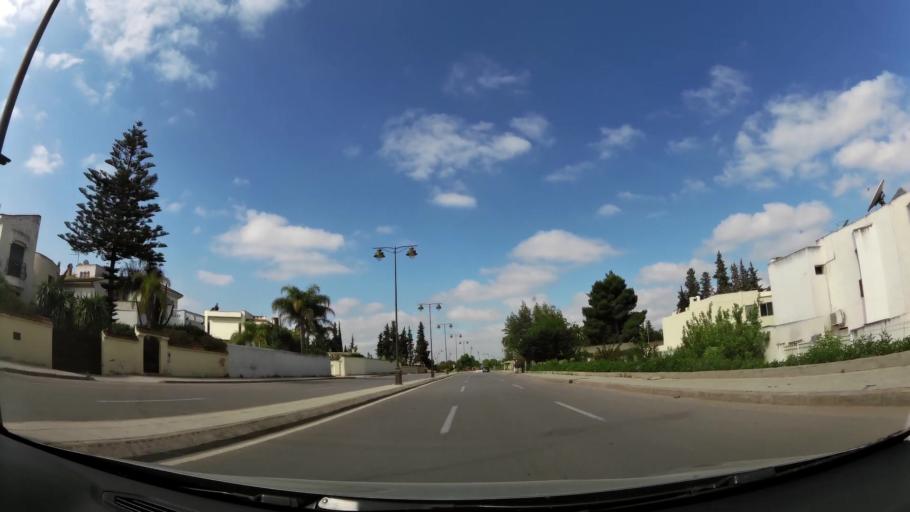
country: MA
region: Fes-Boulemane
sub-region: Fes
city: Fes
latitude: 34.0298
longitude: -5.0161
